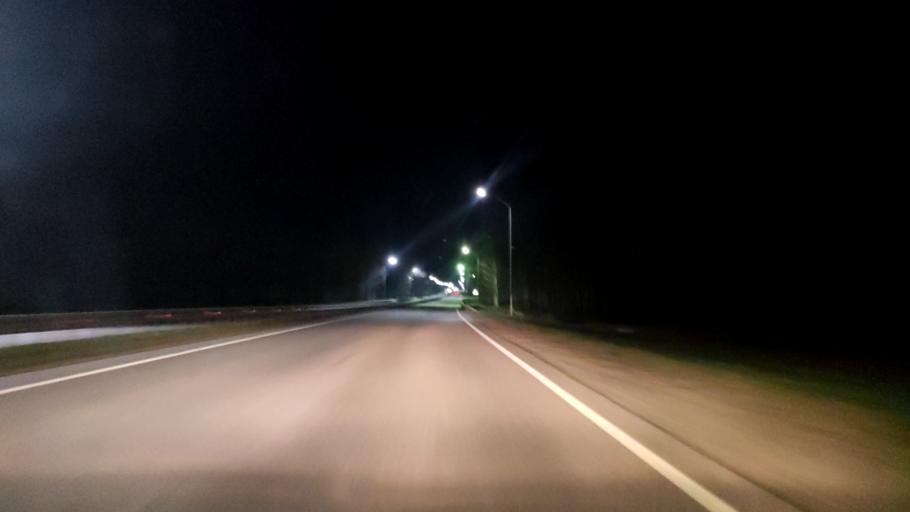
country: RU
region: Belgorod
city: Staryy Oskol
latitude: 51.4071
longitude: 37.8808
